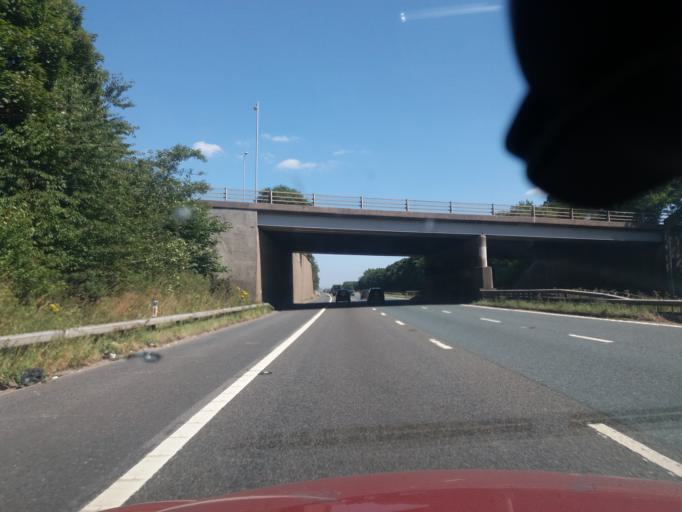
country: GB
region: England
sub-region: Borough of Wigan
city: Atherton
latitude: 53.5491
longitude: -2.4697
